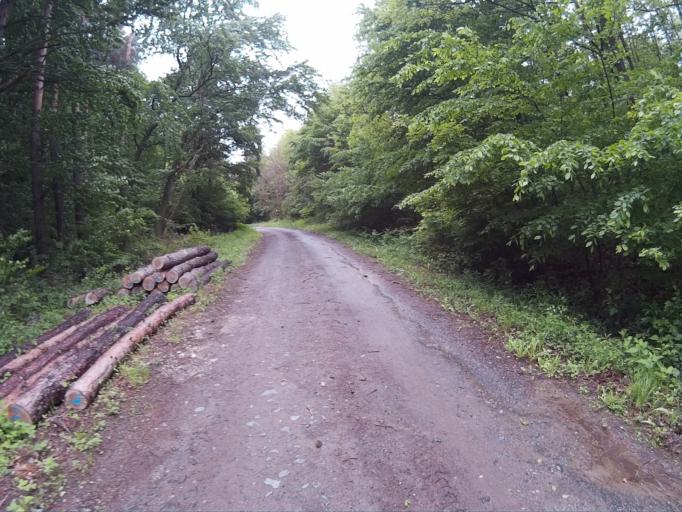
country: HU
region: Veszprem
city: Sumeg
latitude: 46.9110
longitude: 17.2790
